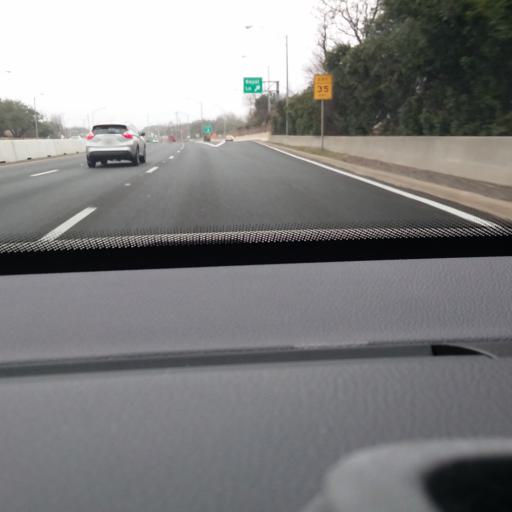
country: US
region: Texas
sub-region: Dallas County
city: University Park
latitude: 32.8619
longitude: -96.7939
